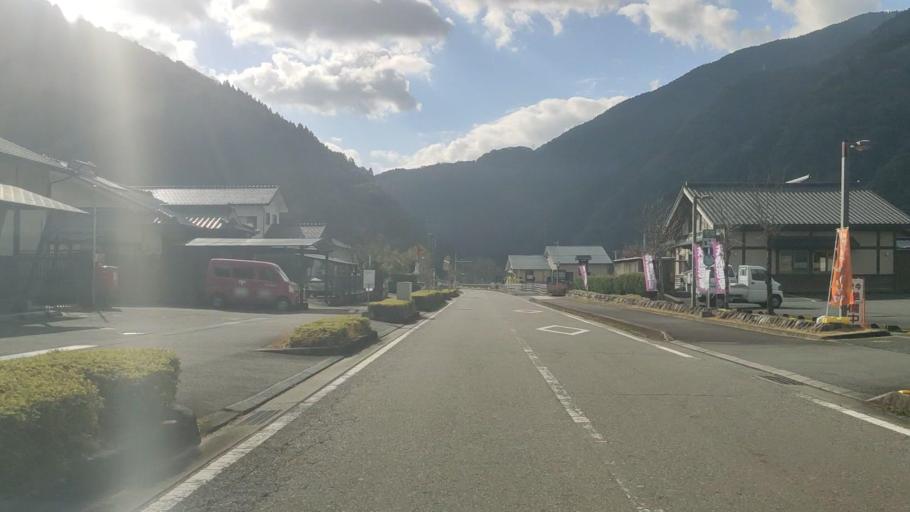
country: JP
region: Kumamoto
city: Hitoyoshi
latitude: 32.3975
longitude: 130.8266
